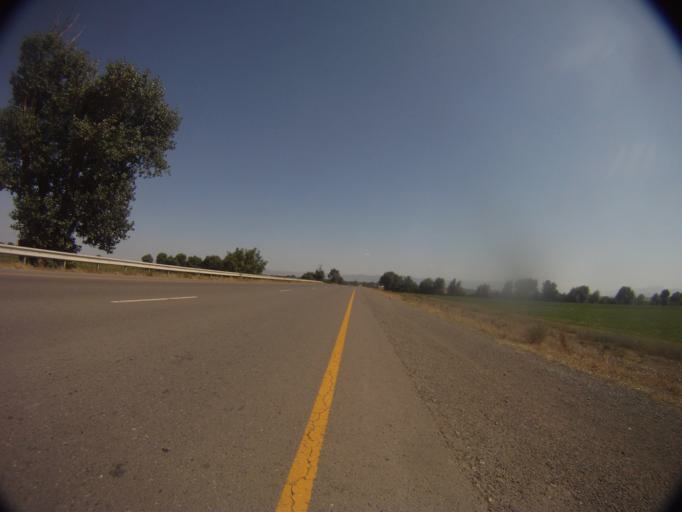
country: AZ
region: Qazax
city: Qazax
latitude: 41.1727
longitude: 45.3068
